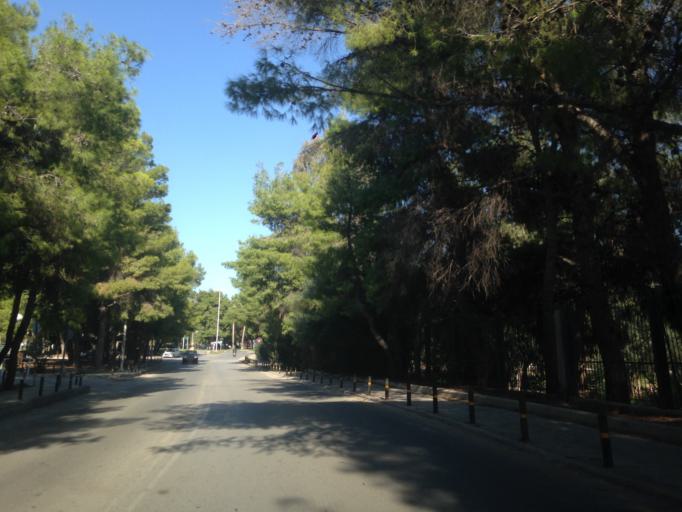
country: GR
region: Attica
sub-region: Nomarchia Anatolikis Attikis
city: Vouliagmeni
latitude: 37.8138
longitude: 23.7779
